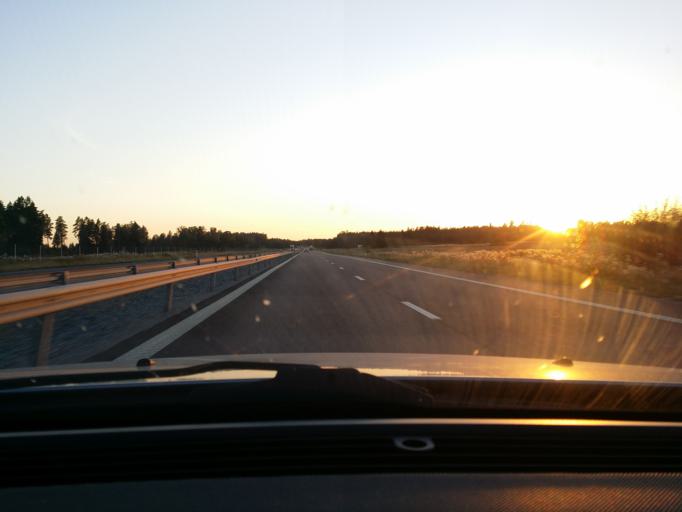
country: SE
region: Vaestmanland
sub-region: Vasteras
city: Tillberga
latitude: 59.6246
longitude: 16.7350
